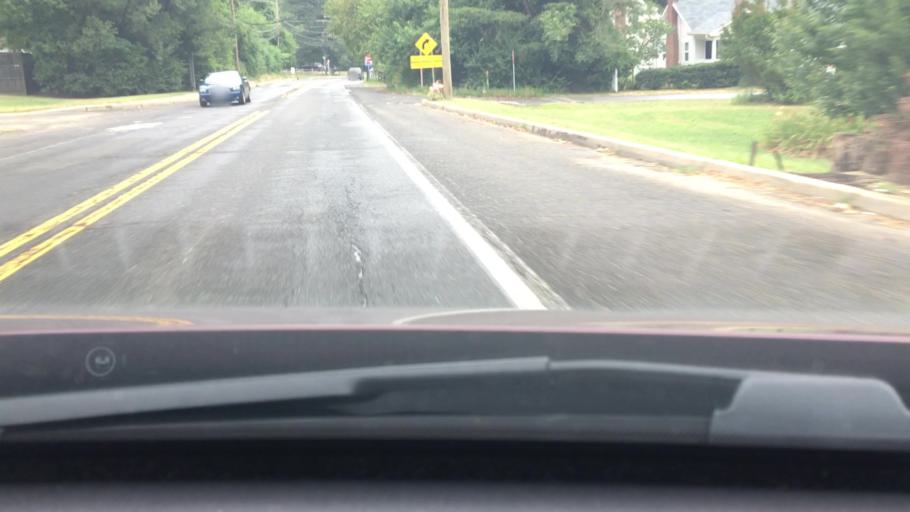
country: US
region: Maryland
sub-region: Prince George's County
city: Beltsville
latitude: 39.0449
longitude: -76.9135
